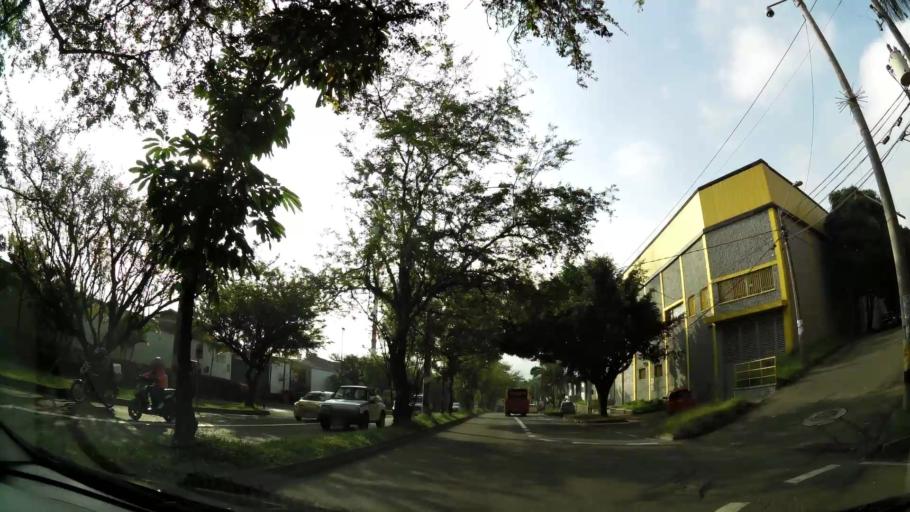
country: CO
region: Antioquia
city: Sabaneta
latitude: 6.1649
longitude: -75.6165
